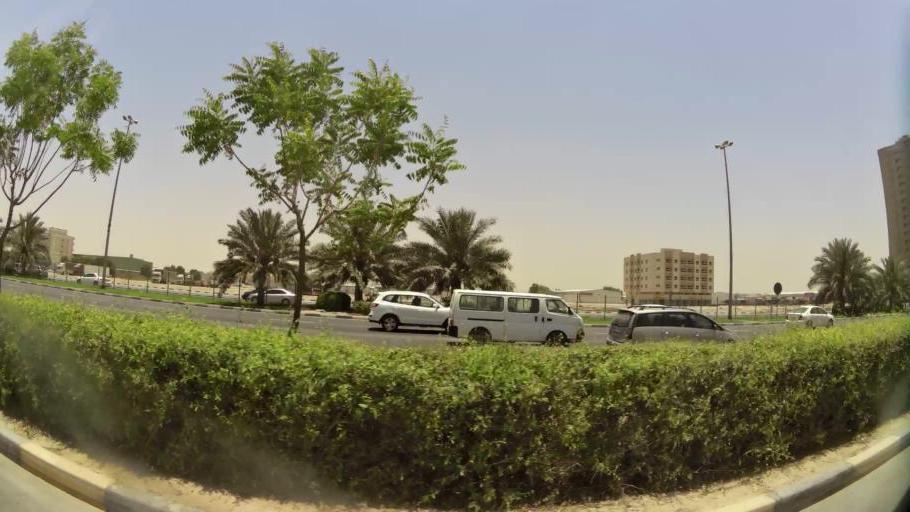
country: AE
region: Ajman
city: Ajman
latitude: 25.3953
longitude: 55.4874
